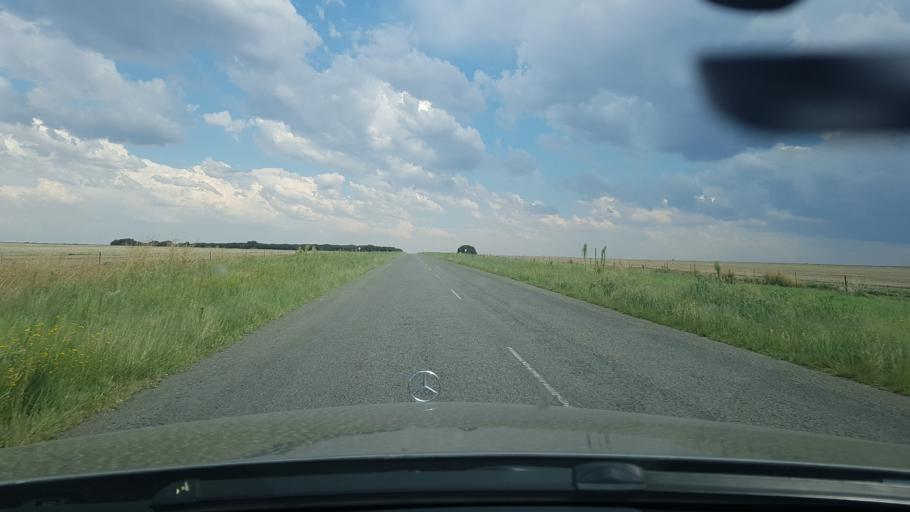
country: ZA
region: North-West
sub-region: Dr Ruth Segomotsi Mompati District Municipality
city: Bloemhof
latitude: -27.8630
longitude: 25.6543
